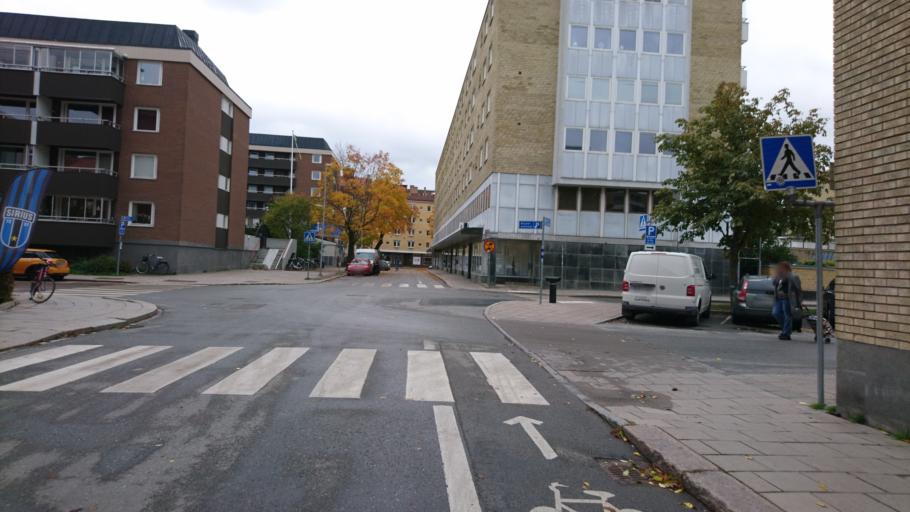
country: SE
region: Uppsala
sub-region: Uppsala Kommun
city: Uppsala
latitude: 59.8619
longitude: 17.6282
